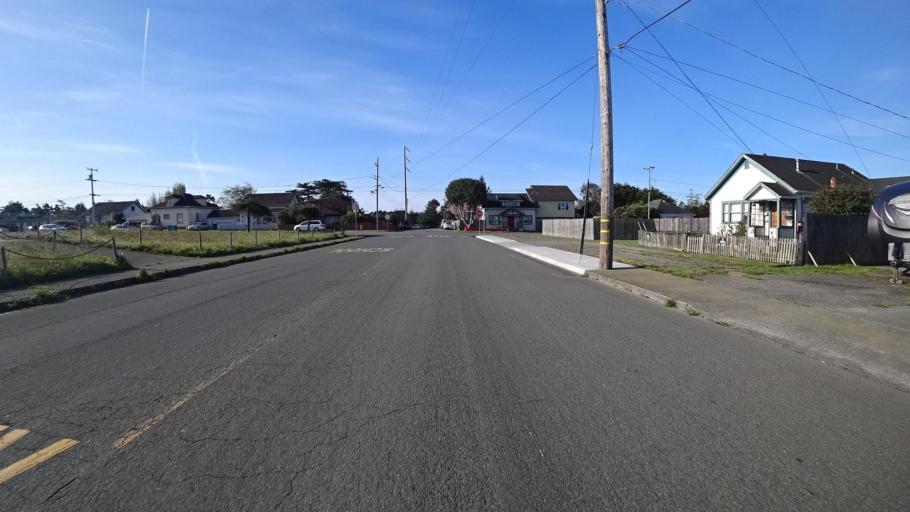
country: US
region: California
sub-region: Humboldt County
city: Bayview
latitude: 40.7737
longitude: -124.1801
